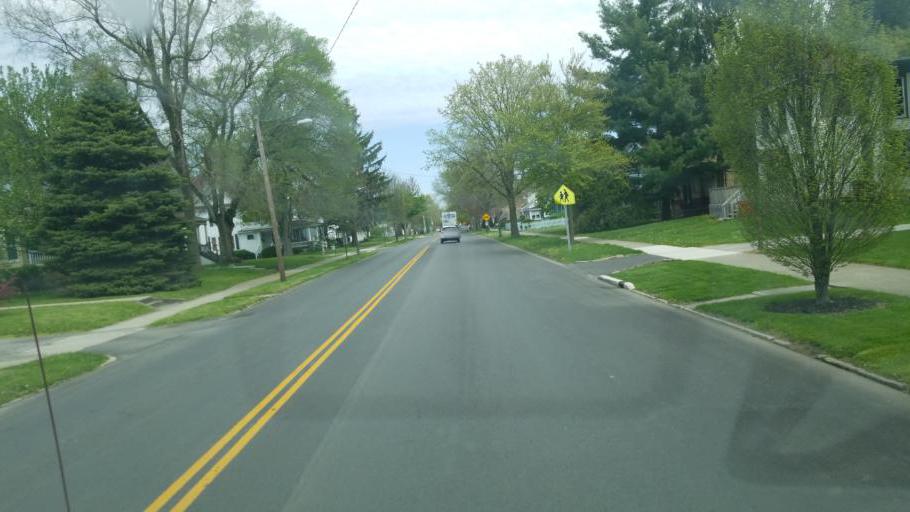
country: US
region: Ohio
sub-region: Hardin County
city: Ada
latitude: 40.7741
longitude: -83.8232
